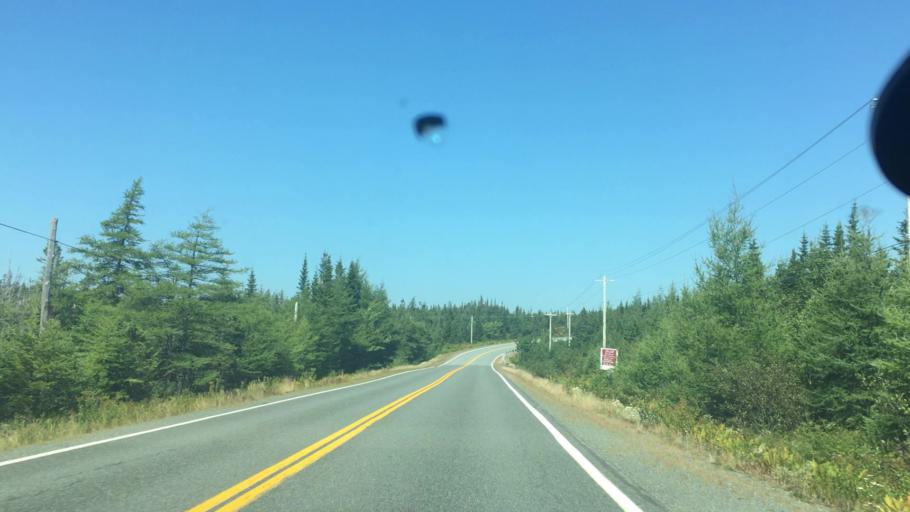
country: CA
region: Nova Scotia
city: Antigonish
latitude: 45.0064
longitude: -62.1045
